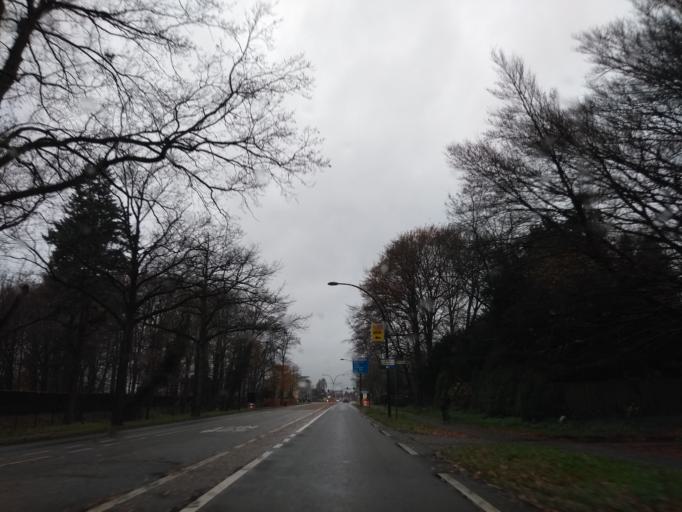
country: NL
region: Overijssel
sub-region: Gemeente Hengelo
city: Hengelo
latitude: 52.2554
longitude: 6.8144
